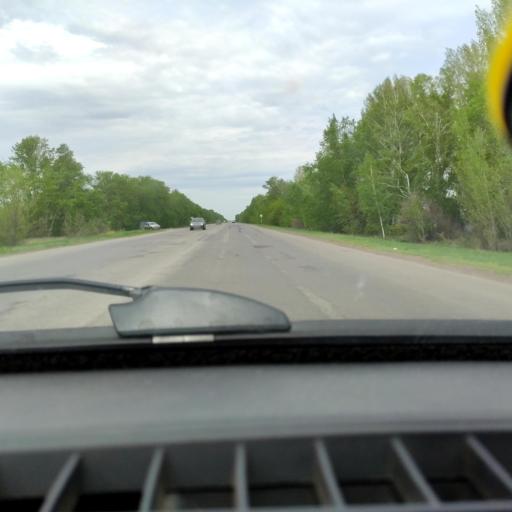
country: RU
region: Samara
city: Tol'yatti
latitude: 53.6328
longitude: 49.4180
